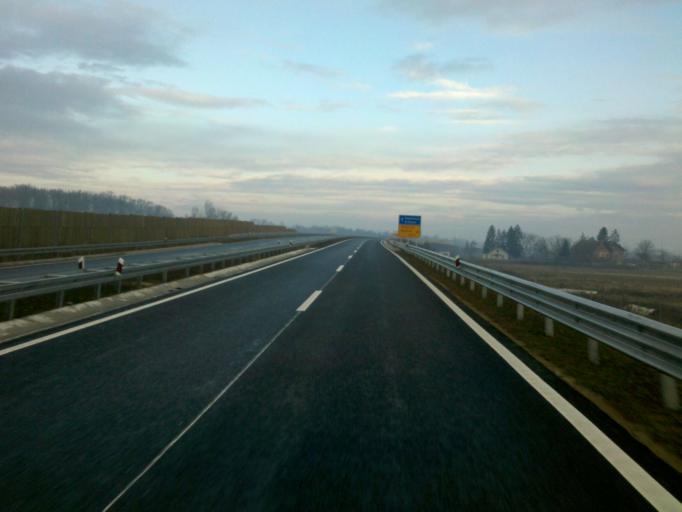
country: HR
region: Zagrebacka
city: Dubrava
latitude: 45.9097
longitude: 16.5038
